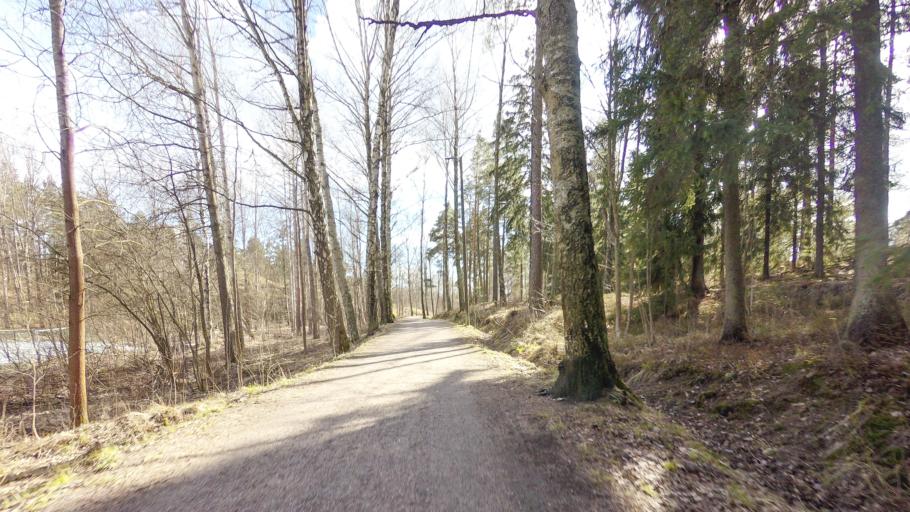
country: FI
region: Uusimaa
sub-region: Helsinki
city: Vantaa
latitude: 60.2079
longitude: 25.0318
